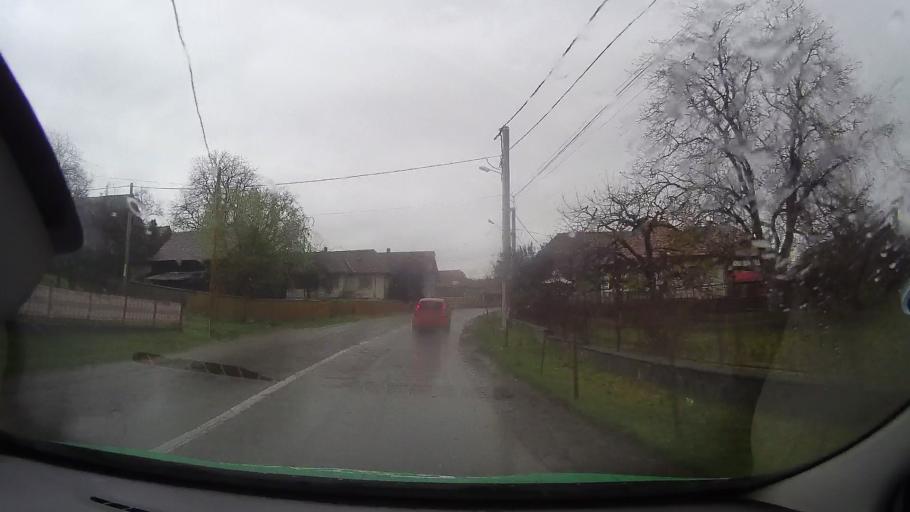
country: RO
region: Mures
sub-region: Comuna Vatava
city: Vatava
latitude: 46.9414
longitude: 24.7657
